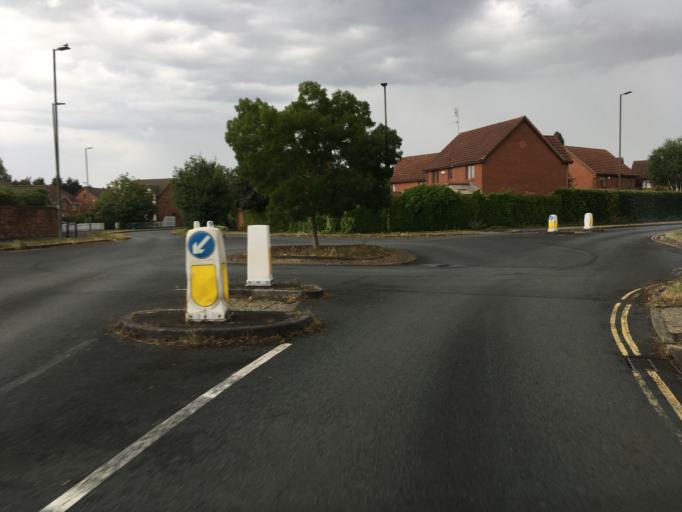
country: GB
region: England
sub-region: Gloucestershire
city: Barnwood
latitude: 51.8492
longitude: -2.1800
